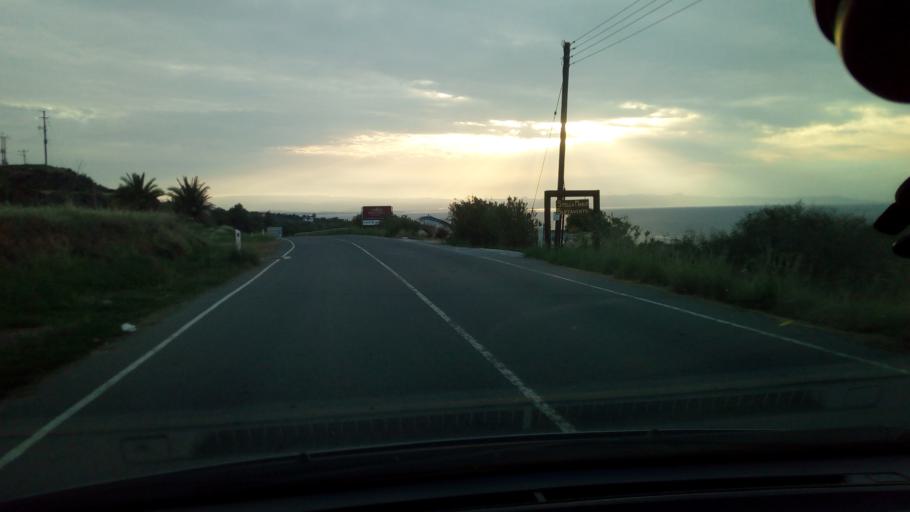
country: CY
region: Pafos
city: Polis
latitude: 35.1459
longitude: 32.5298
